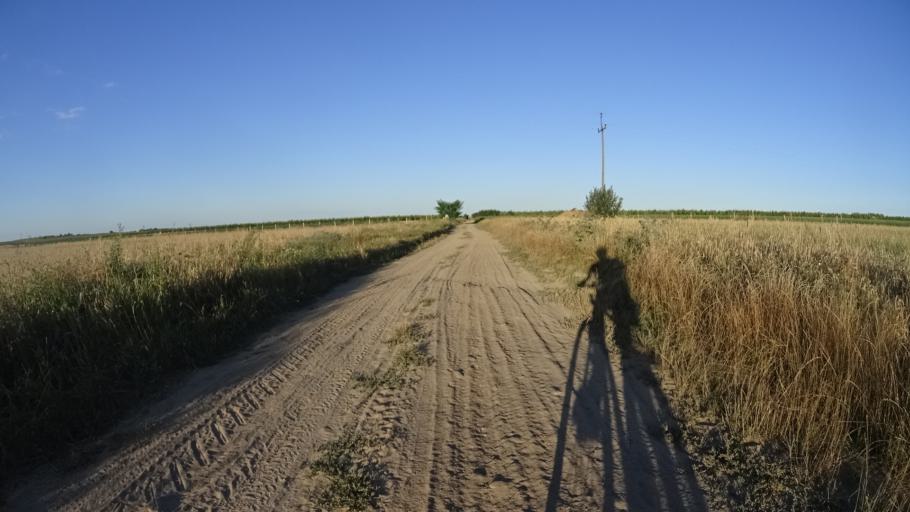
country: PL
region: Masovian Voivodeship
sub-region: Powiat bialobrzeski
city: Wysmierzyce
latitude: 51.6596
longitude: 20.8025
